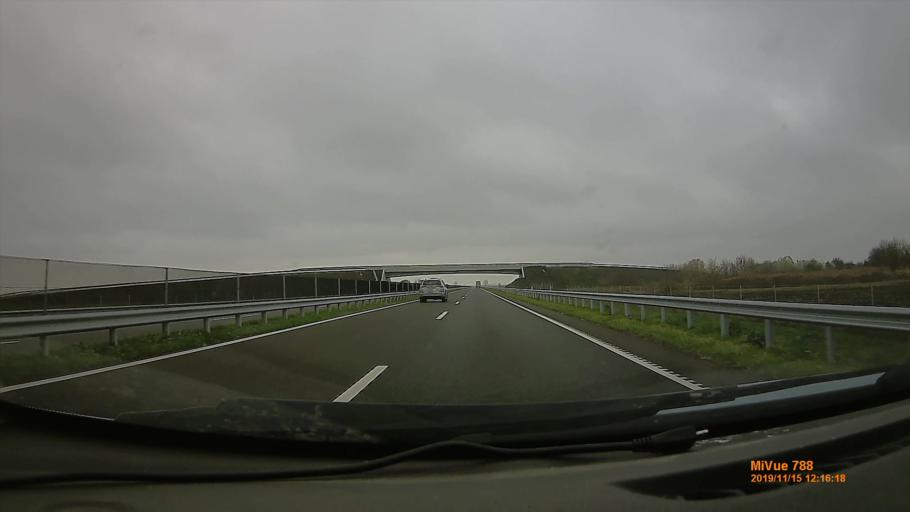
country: HU
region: Bekes
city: Szarvas
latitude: 46.8179
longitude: 20.5603
